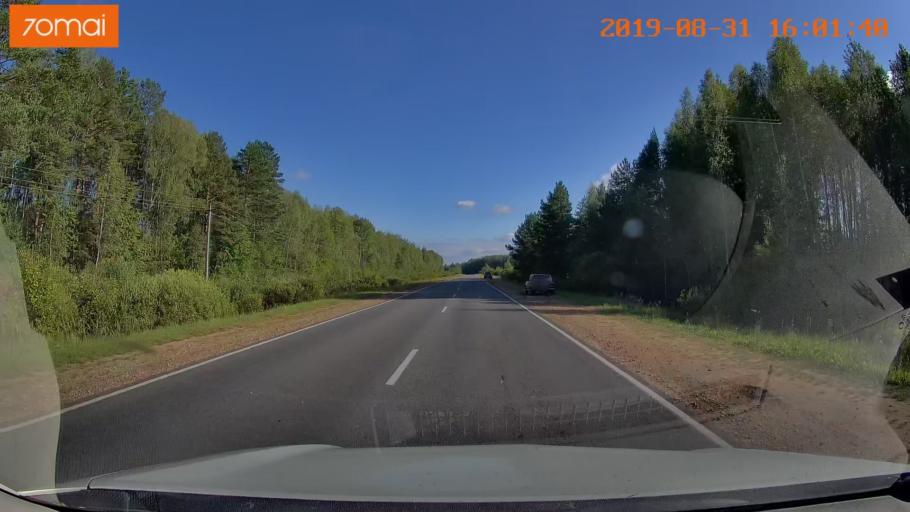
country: RU
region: Kaluga
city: Yukhnov
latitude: 54.6859
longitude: 35.2922
